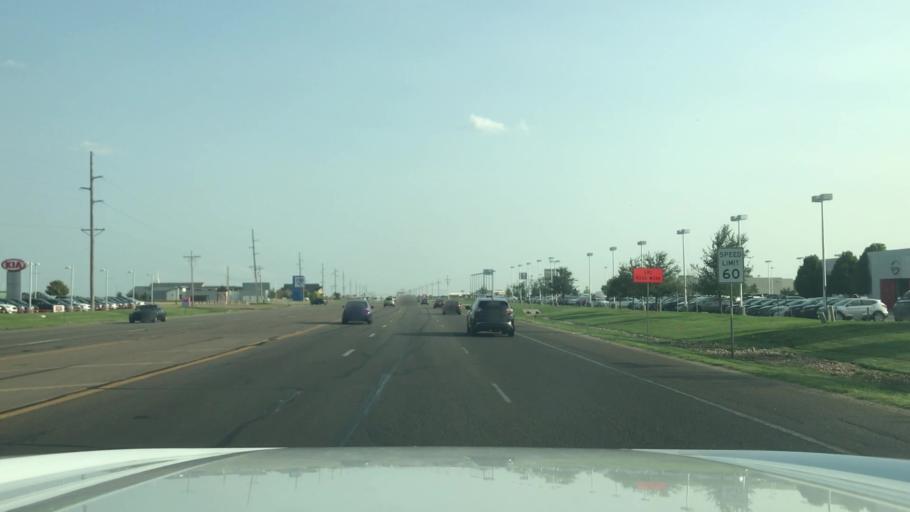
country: US
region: Texas
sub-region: Potter County
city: Amarillo
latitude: 35.1601
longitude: -101.9382
